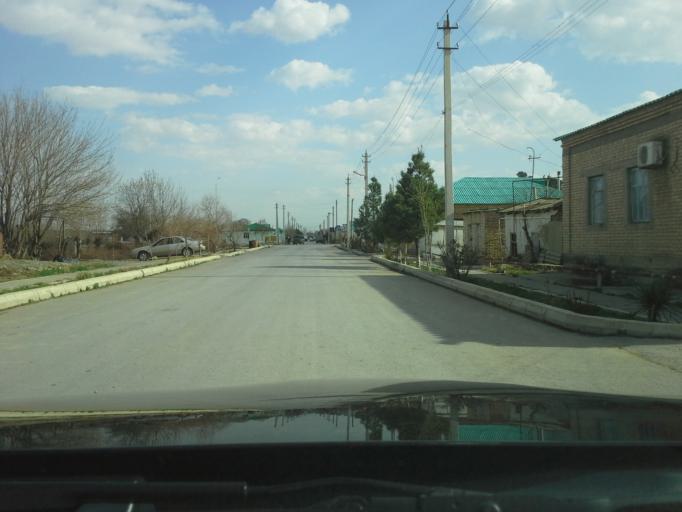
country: TM
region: Ahal
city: Ashgabat
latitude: 37.9902
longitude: 58.2866
